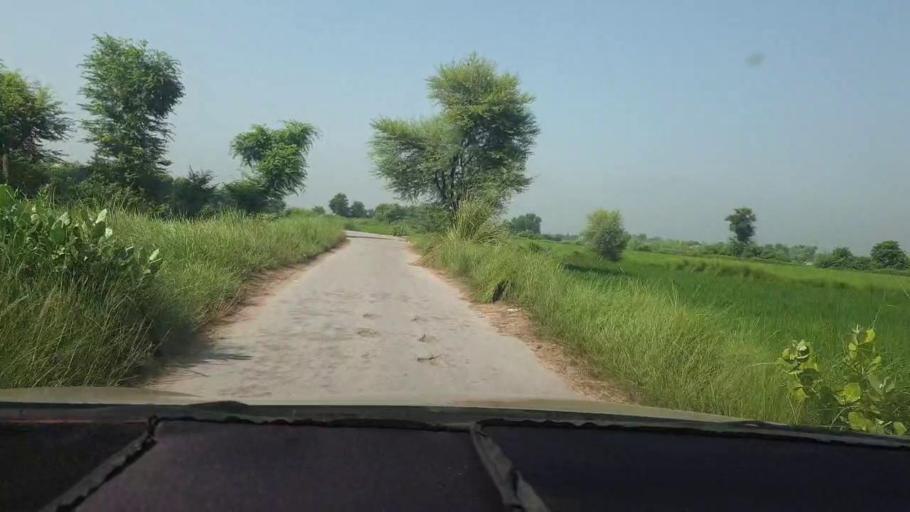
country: PK
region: Sindh
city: Kambar
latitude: 27.5818
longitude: 68.0557
